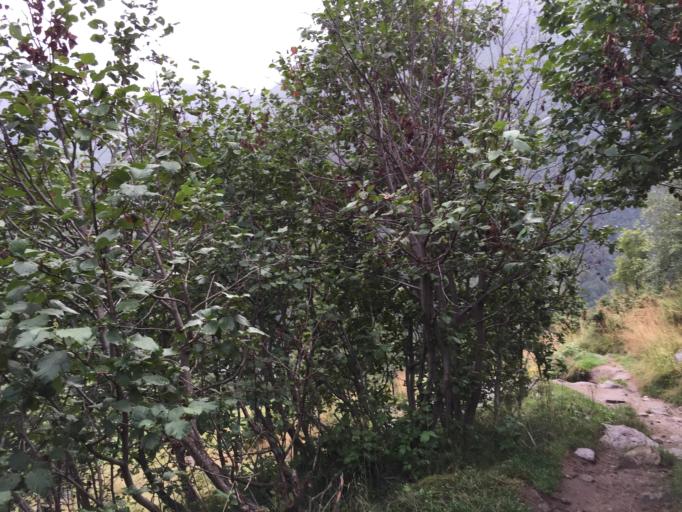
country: NO
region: More og Romsdal
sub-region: Norddal
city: Valldal
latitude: 62.1010
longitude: 7.2238
